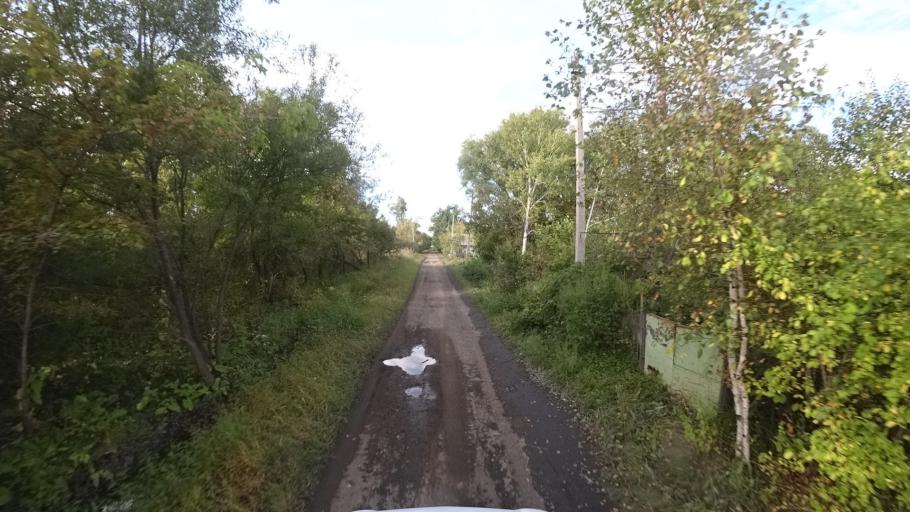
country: RU
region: Primorskiy
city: Dostoyevka
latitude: 44.2922
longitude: 133.4301
